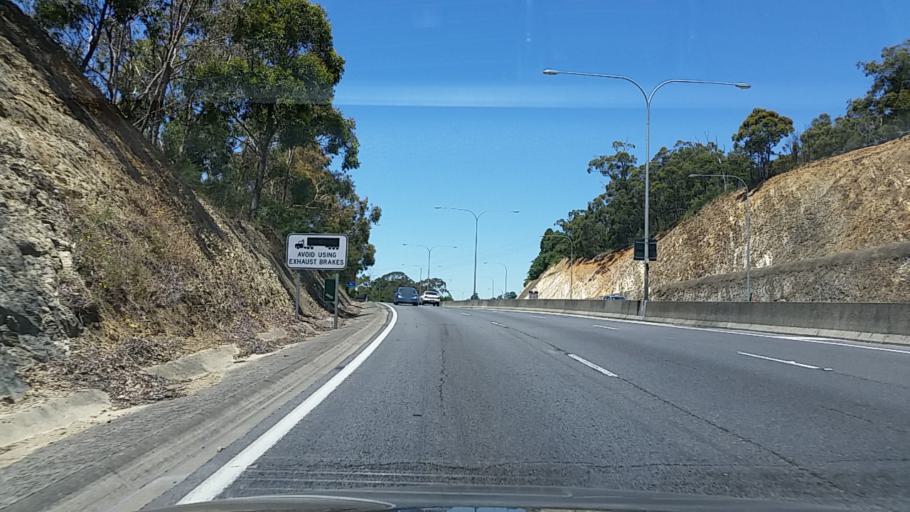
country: AU
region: South Australia
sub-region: Adelaide Hills
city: Crafers
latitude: -34.9938
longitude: 138.6972
